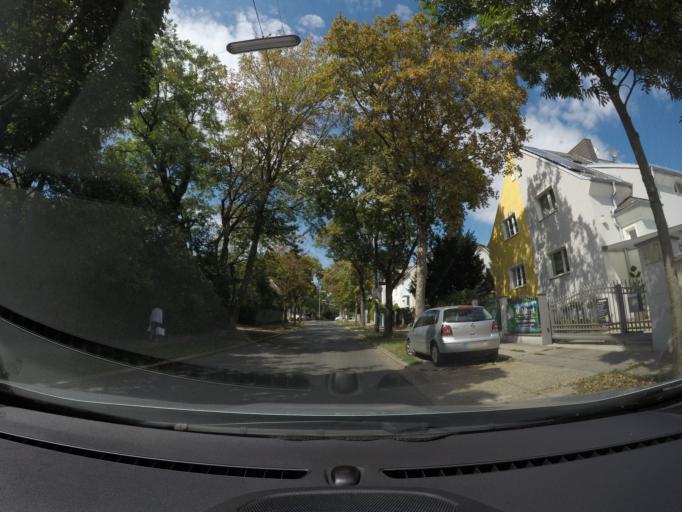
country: AT
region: Lower Austria
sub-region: Politischer Bezirk Modling
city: Perchtoldsdorf
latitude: 48.1817
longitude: 16.2648
